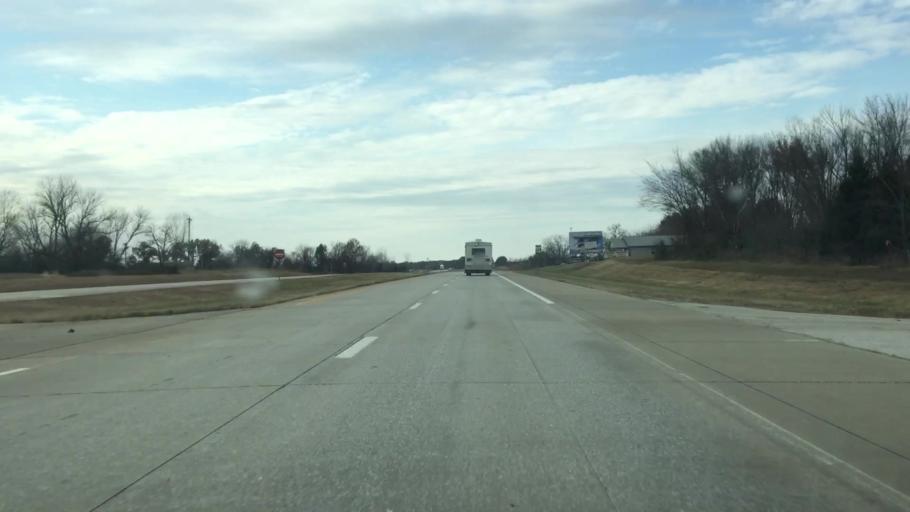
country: US
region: Missouri
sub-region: Henry County
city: Clinton
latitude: 38.4344
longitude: -93.9336
